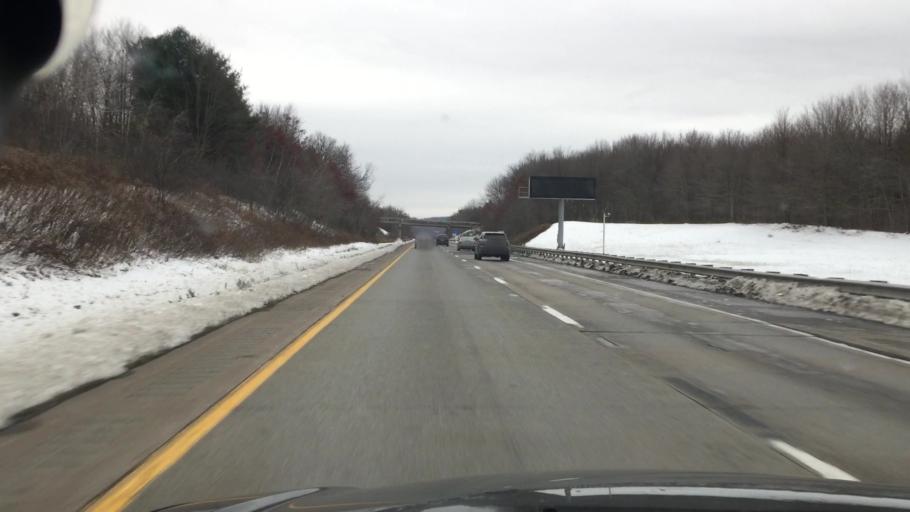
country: US
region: Pennsylvania
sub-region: Luzerne County
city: Nanticoke
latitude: 41.1243
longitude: -75.9624
